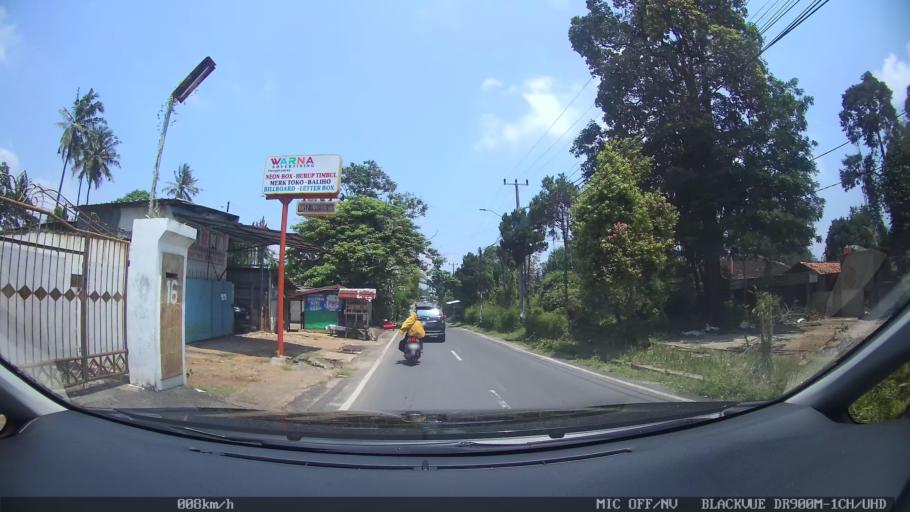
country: ID
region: Lampung
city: Kedaton
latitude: -5.3739
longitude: 105.2693
